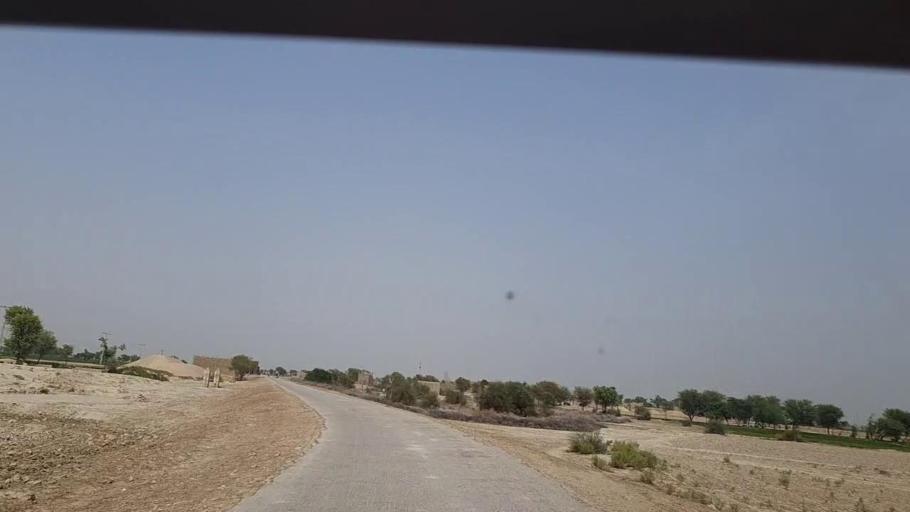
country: PK
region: Sindh
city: Khairpur Nathan Shah
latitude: 27.0231
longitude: 67.5886
